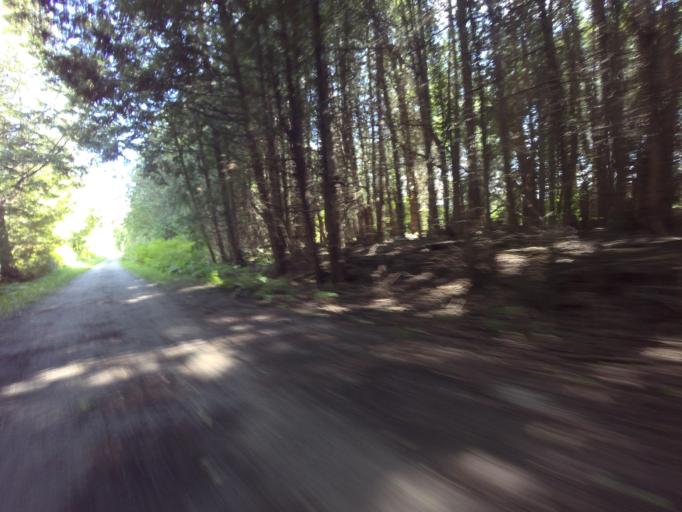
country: CA
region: Ontario
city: Orangeville
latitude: 43.7851
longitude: -80.1516
